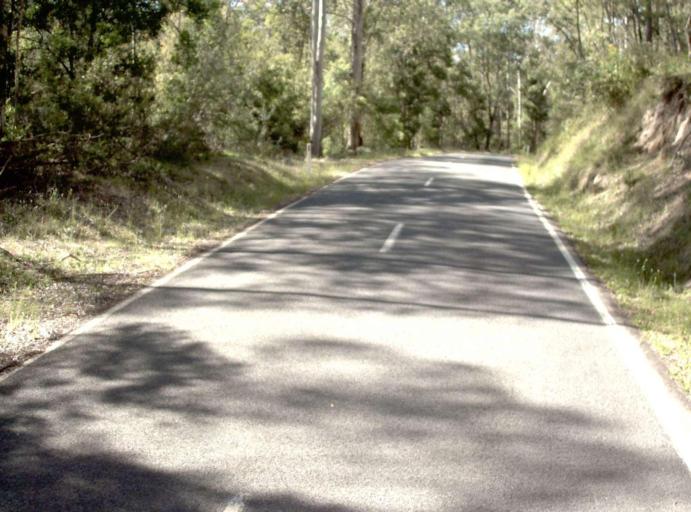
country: AU
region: New South Wales
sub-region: Bombala
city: Bombala
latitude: -37.3587
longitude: 148.6836
